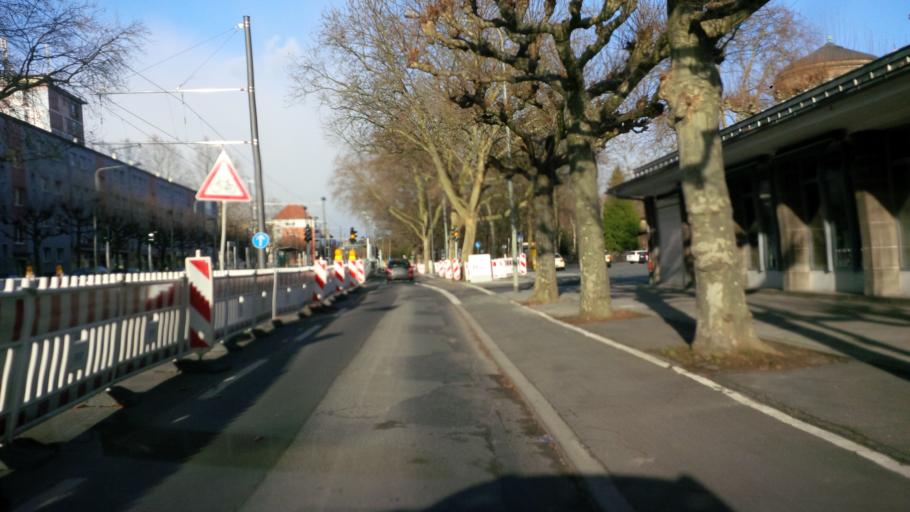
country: DE
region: Hesse
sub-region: Regierungsbezirk Darmstadt
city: Frankfurt am Main
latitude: 50.1353
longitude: 8.6842
